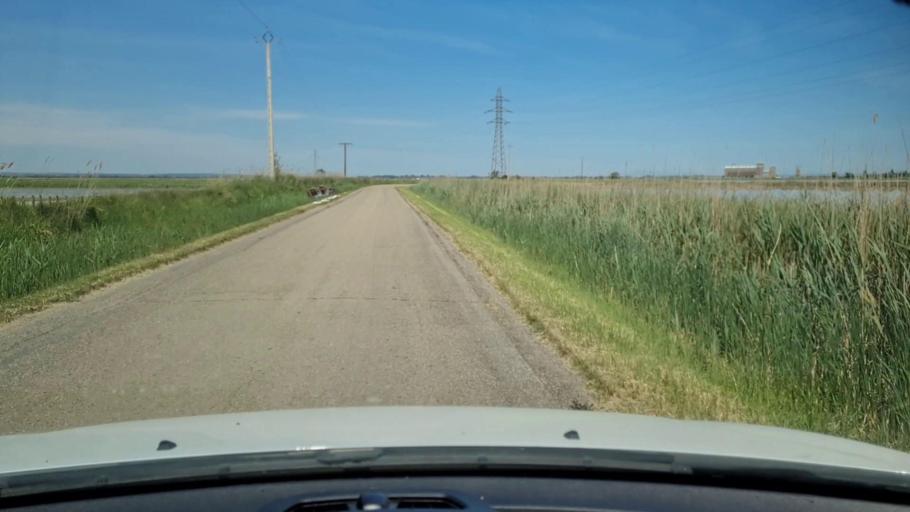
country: FR
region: Languedoc-Roussillon
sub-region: Departement du Gard
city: Saint-Gilles
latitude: 43.5782
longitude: 4.3984
